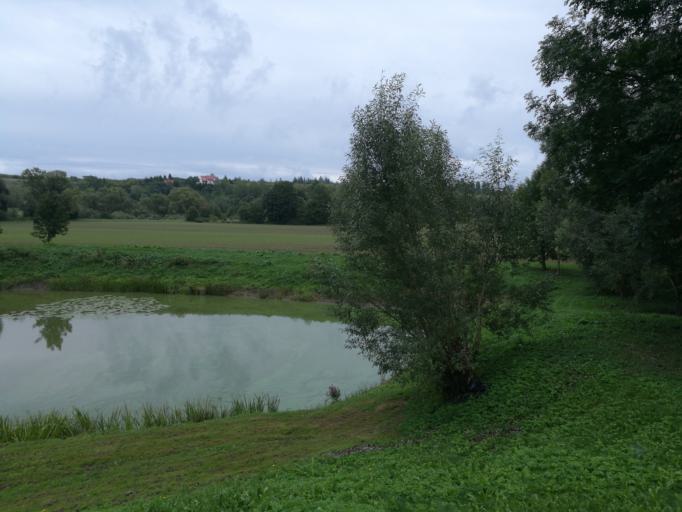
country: LT
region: Kauno apskritis
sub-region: Kaunas
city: Sargenai
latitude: 55.0650
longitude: 23.7933
